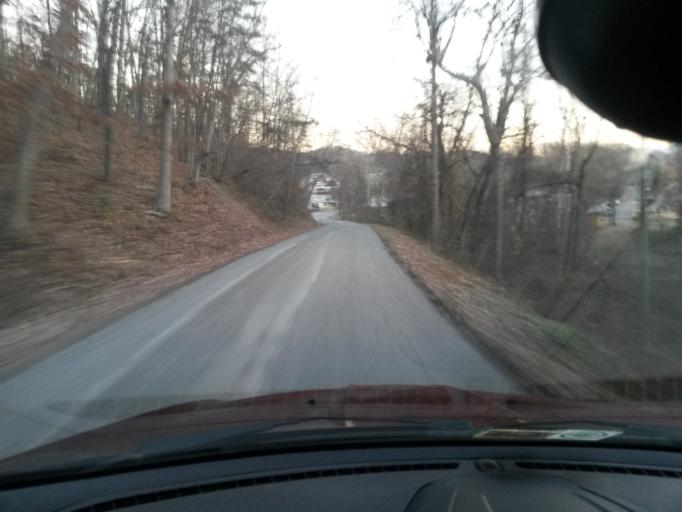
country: US
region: Virginia
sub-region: Alleghany County
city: Clifton Forge
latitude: 37.8216
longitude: -79.7992
